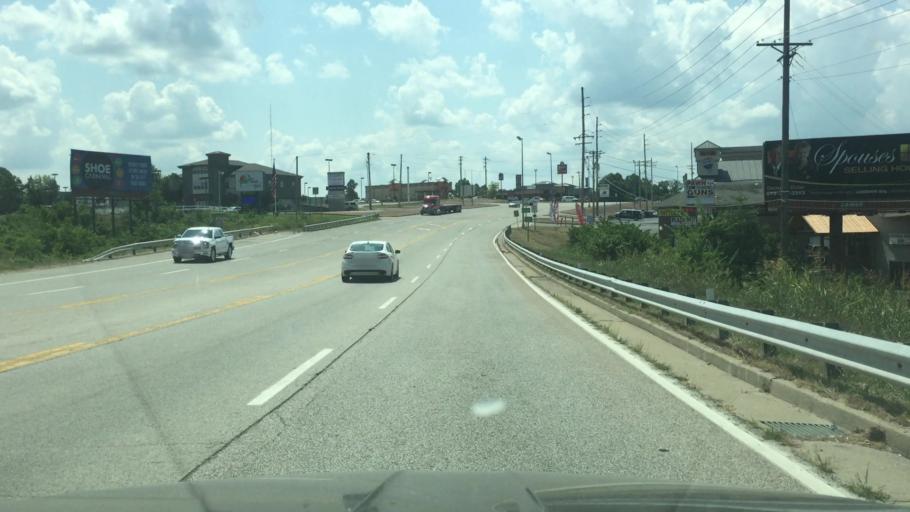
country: US
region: Missouri
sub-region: Miller County
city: Lake Ozark
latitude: 38.1716
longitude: -92.6129
